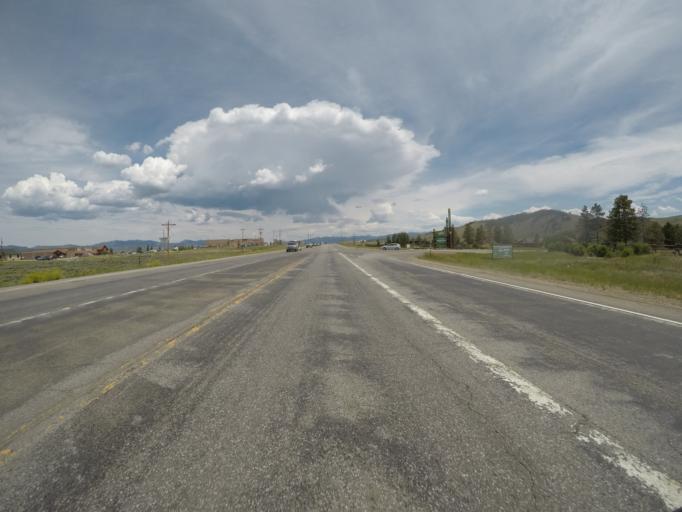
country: US
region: Colorado
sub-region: Grand County
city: Granby
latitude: 40.0601
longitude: -105.9277
